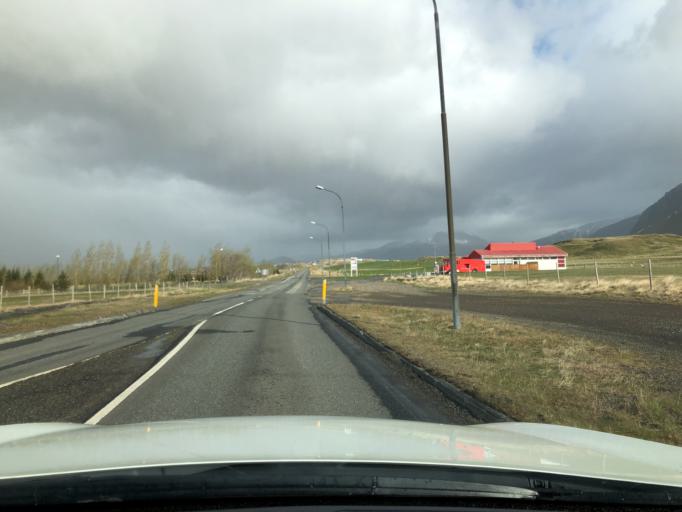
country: IS
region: East
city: Hoefn
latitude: 64.3125
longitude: -15.2286
